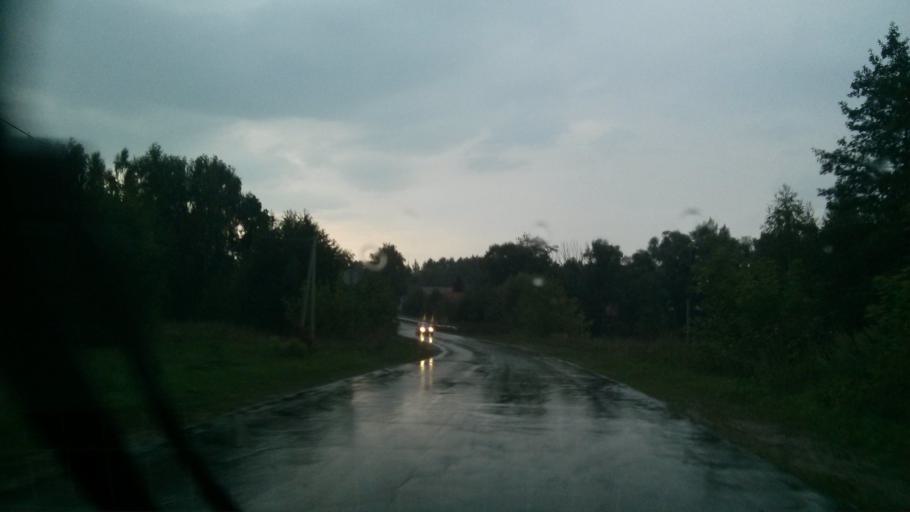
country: RU
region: Nizjnij Novgorod
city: Shimorskoye
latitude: 55.3453
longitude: 41.9300
